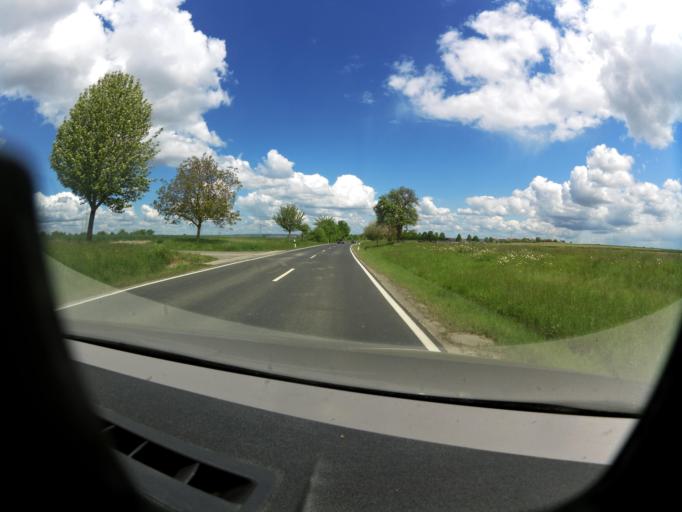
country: DE
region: Bavaria
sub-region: Regierungsbezirk Unterfranken
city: Waigolshausen
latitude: 49.9578
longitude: 10.1477
